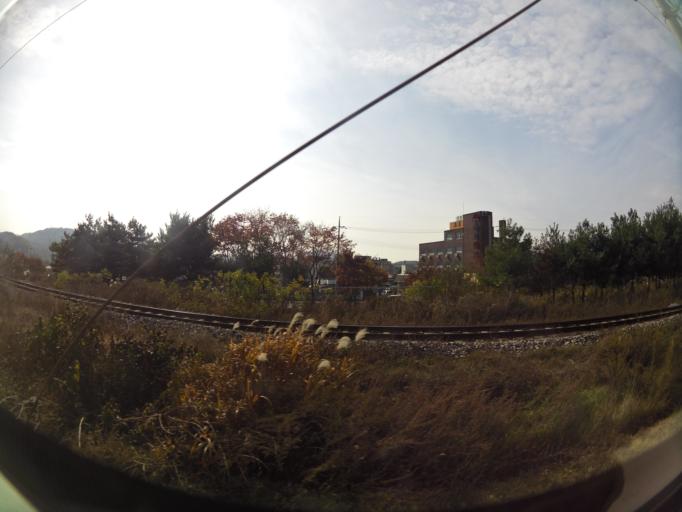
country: KR
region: Daejeon
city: Sintansin
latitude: 36.5306
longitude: 127.3718
